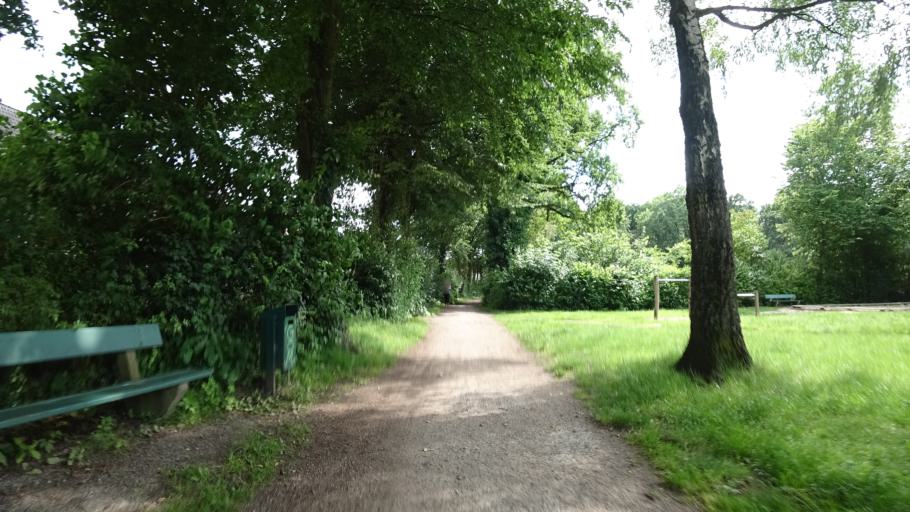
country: DE
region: North Rhine-Westphalia
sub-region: Regierungsbezirk Detmold
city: Guetersloh
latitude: 51.9273
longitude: 8.3797
